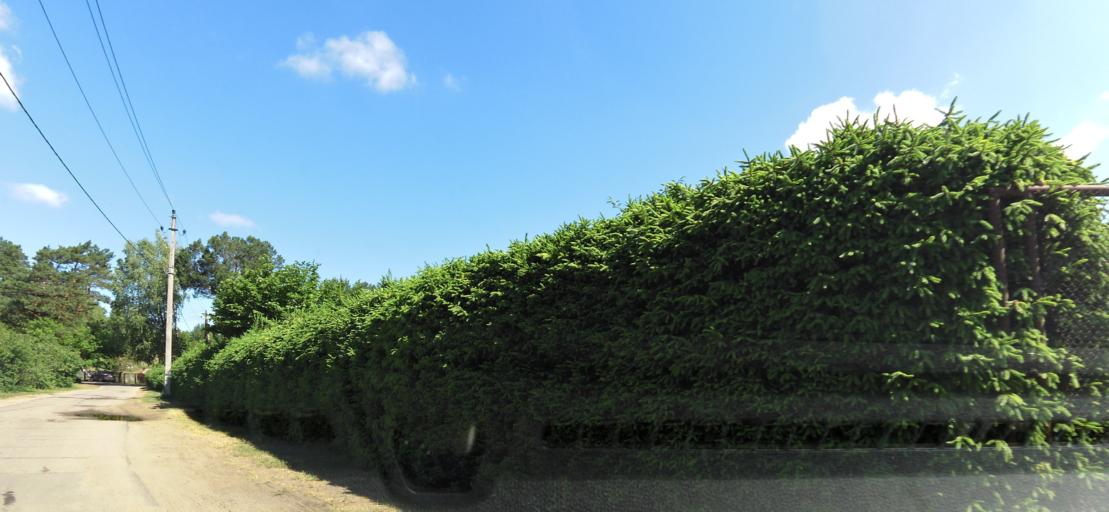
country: LT
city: Nemencine
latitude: 54.7964
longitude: 25.4023
